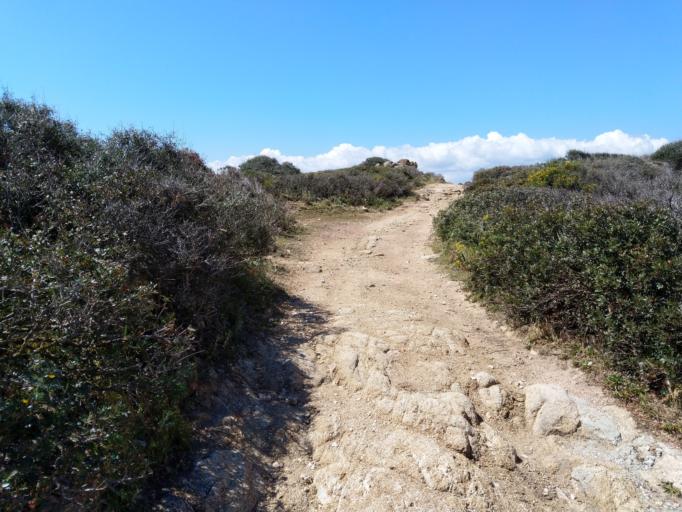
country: IT
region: Sardinia
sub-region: Provincia di Cagliari
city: Olia Speciosa
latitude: 39.2990
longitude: 9.6322
